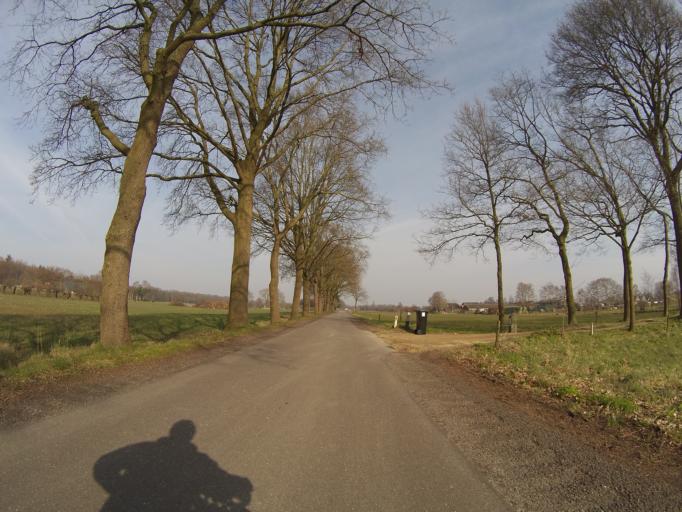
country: NL
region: Gelderland
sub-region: Gemeente Nijkerk
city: Nijkerk
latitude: 52.1864
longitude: 5.4497
